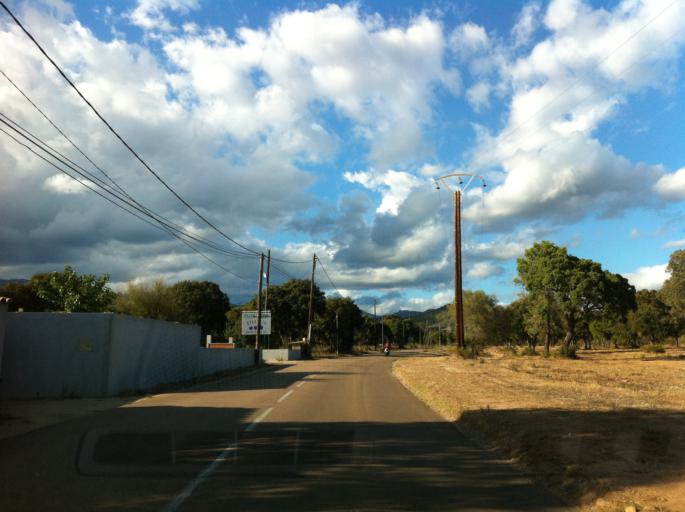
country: FR
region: Corsica
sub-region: Departement de la Corse-du-Sud
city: Porto-Vecchio
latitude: 41.6446
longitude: 9.3291
